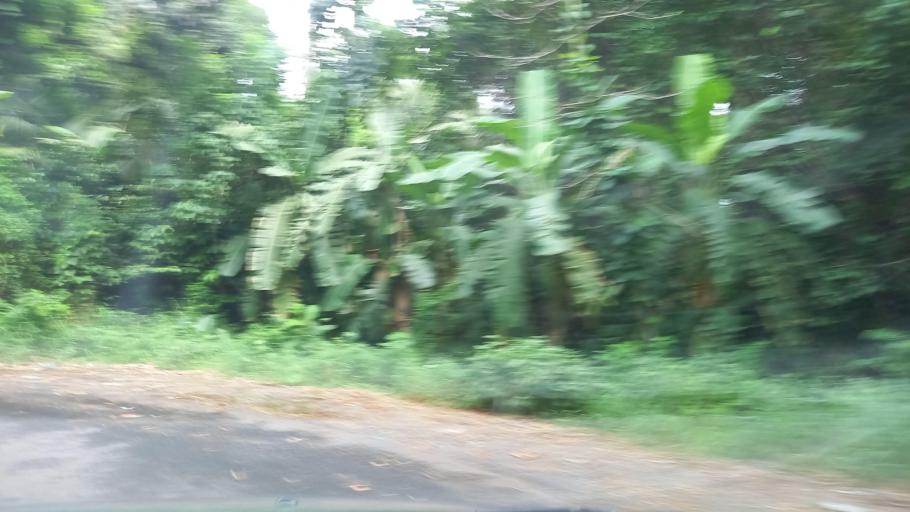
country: YT
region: Ouangani
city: Ouangani
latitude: -12.8418
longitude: 45.1236
